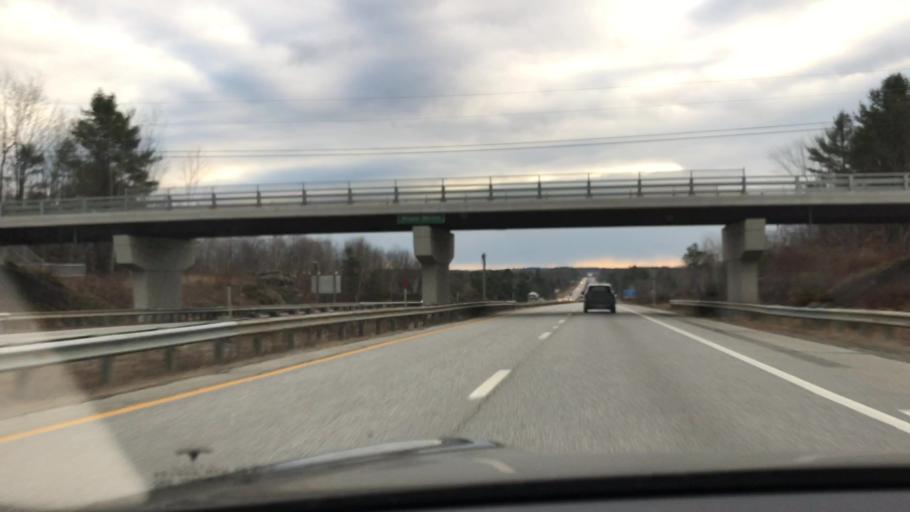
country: US
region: Maine
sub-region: Kennebec County
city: Hallowell
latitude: 44.2644
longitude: -69.8069
